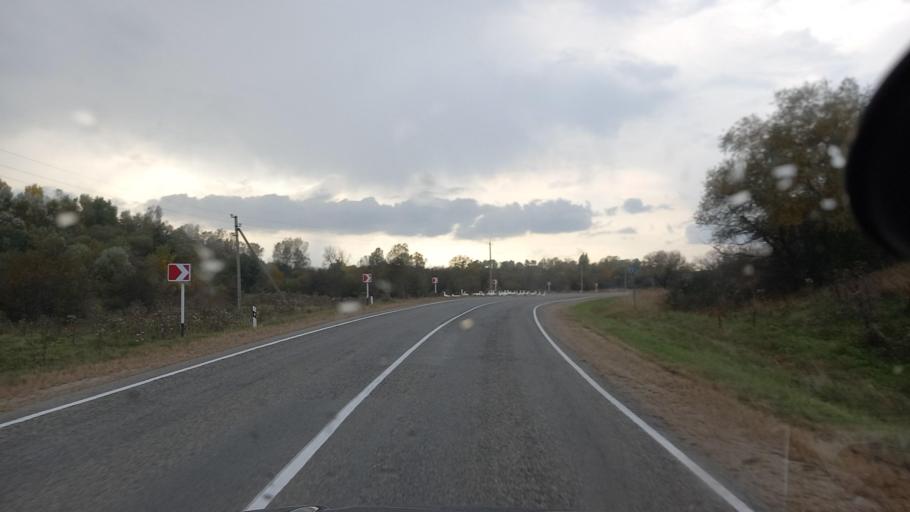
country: RU
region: Krasnodarskiy
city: Perepravnaya
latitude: 44.3724
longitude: 40.7301
